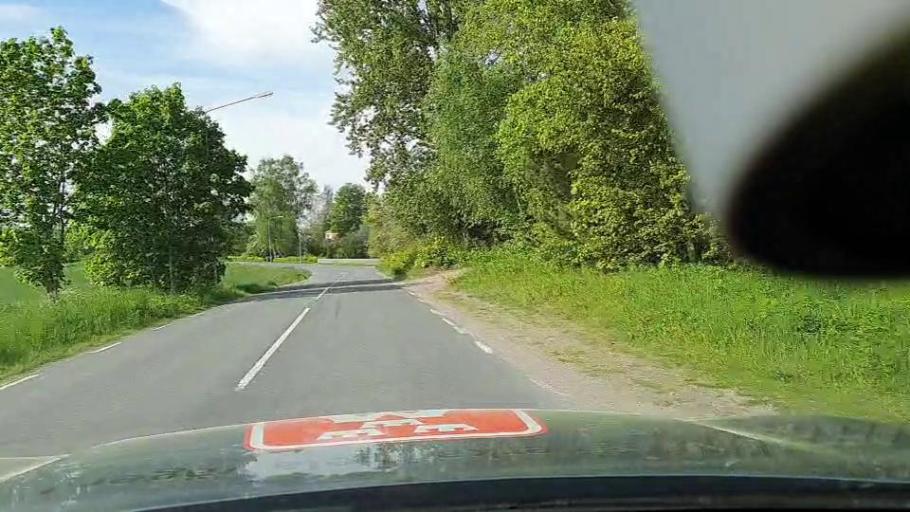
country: SE
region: Soedermanland
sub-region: Eskilstuna Kommun
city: Arla
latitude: 59.2784
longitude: 16.6697
